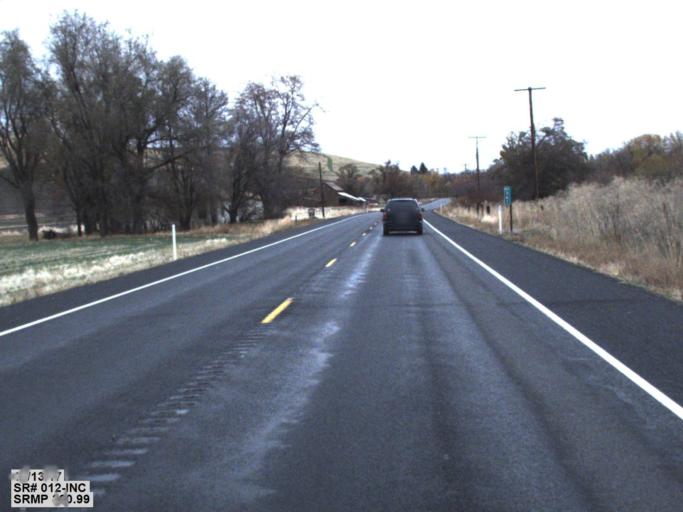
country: US
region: Washington
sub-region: Walla Walla County
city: Waitsburg
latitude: 46.2891
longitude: -118.0917
